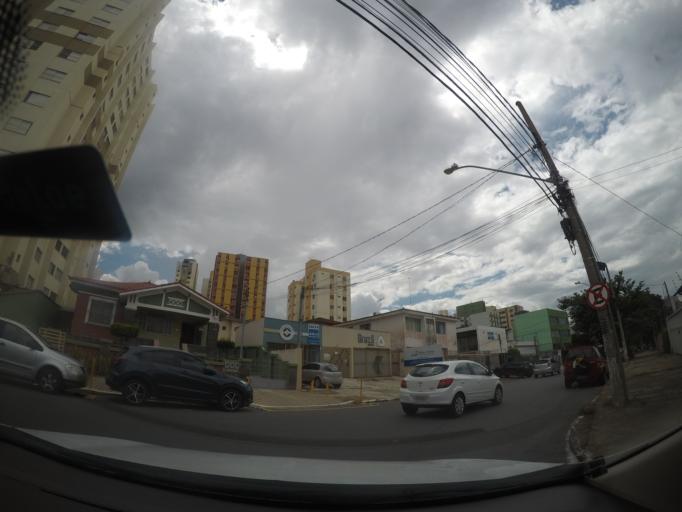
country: BR
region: Goias
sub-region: Goiania
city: Goiania
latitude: -16.6769
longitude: -49.2502
